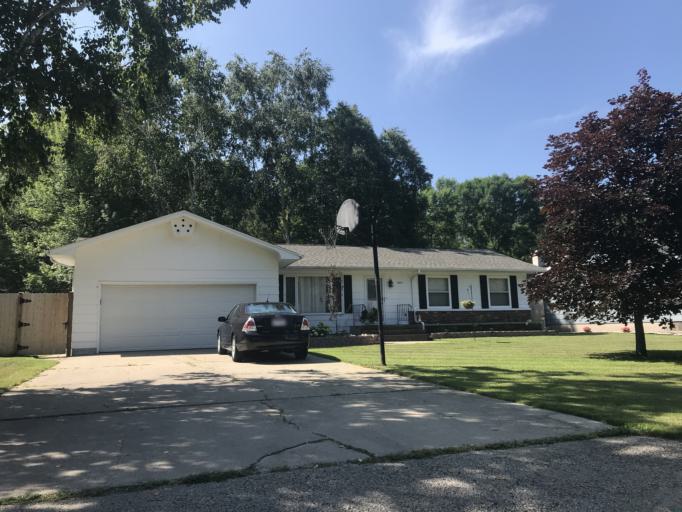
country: US
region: Wisconsin
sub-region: Marinette County
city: Marinette
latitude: 45.0976
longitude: -87.6576
